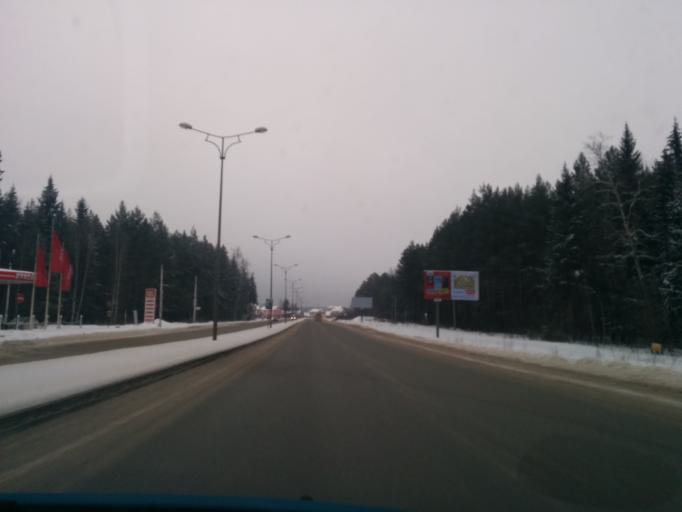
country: RU
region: Perm
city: Kondratovo
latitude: 58.0229
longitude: 55.9953
